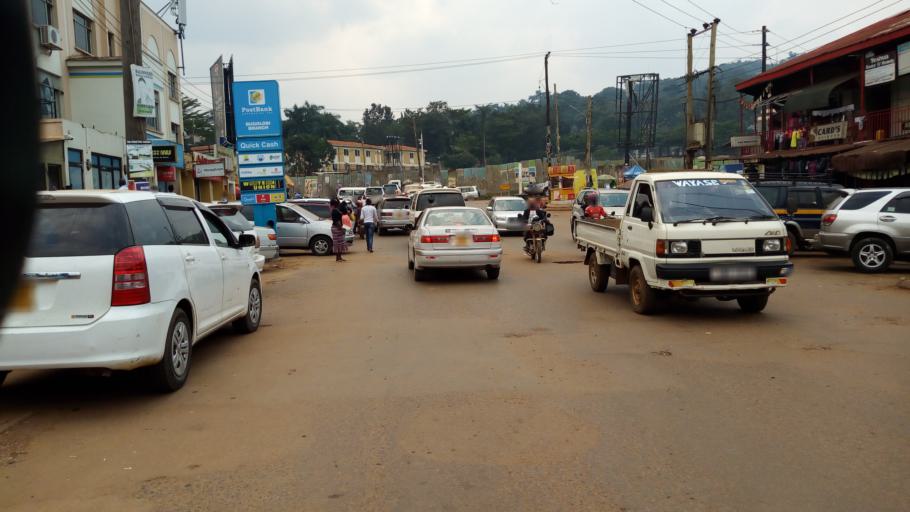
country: UG
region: Central Region
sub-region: Wakiso District
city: Kireka
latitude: 0.3186
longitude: 32.6231
